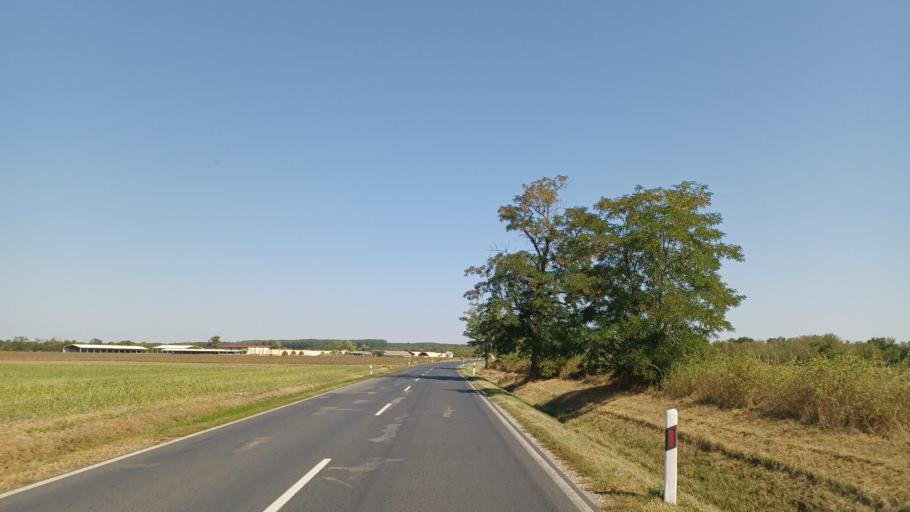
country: HU
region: Tolna
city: Nagydorog
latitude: 46.6675
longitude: 18.6580
